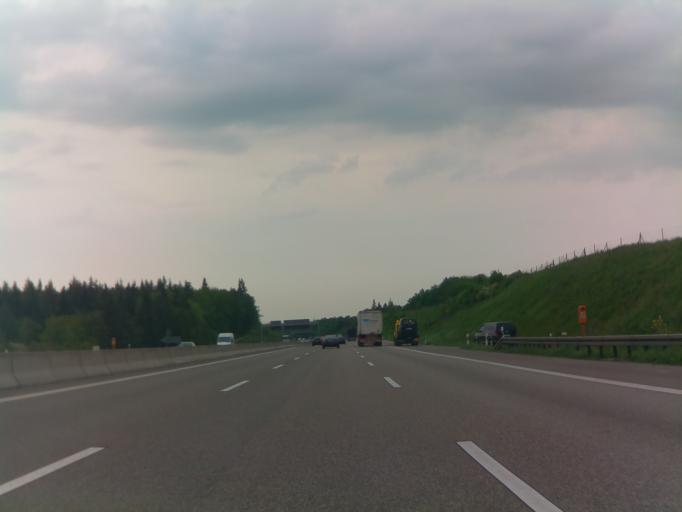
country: DE
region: Baden-Wuerttemberg
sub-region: Karlsruhe Region
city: Wurmberg
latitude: 48.8791
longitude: 8.7885
